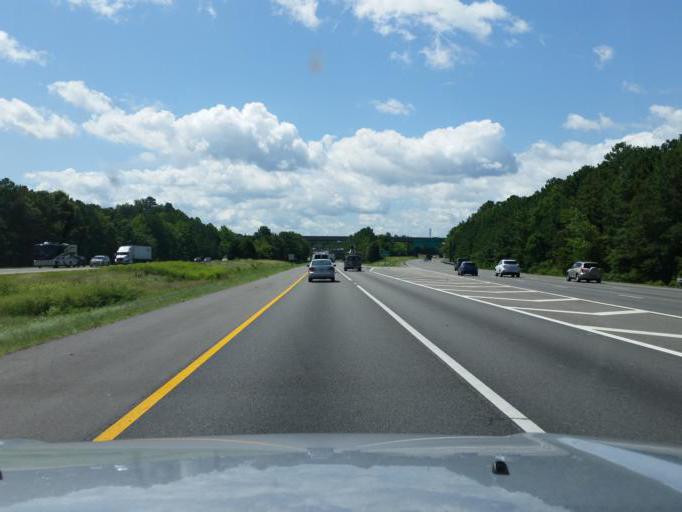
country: US
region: Virginia
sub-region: Henrico County
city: Chamberlayne
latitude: 37.6686
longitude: -77.4482
